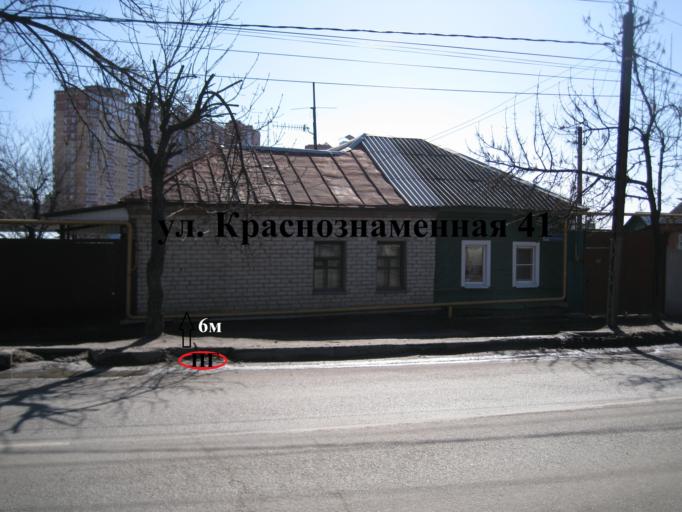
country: RU
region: Voronezj
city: Voronezh
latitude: 51.6498
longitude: 39.1858
